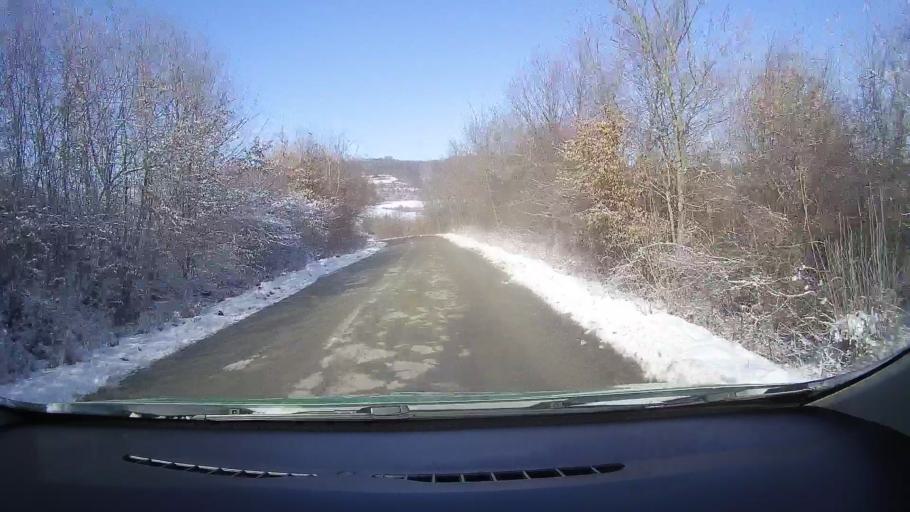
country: RO
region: Sibiu
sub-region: Comuna Altina
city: Altina
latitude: 45.9916
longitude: 24.4338
